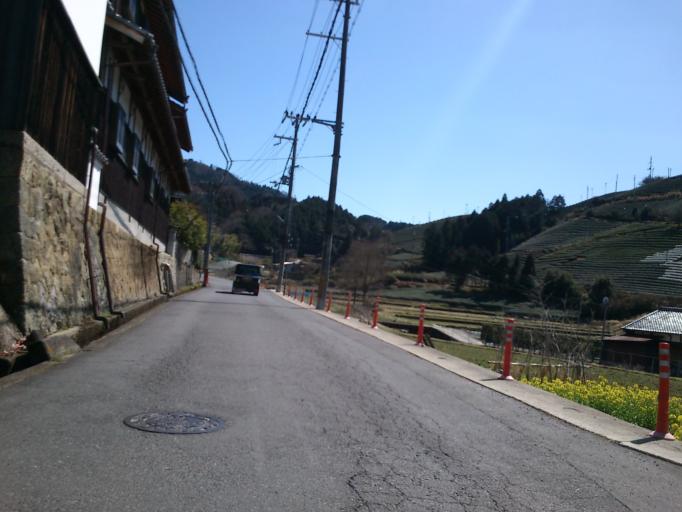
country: JP
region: Nara
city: Nara-shi
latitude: 34.7851
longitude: 135.9075
